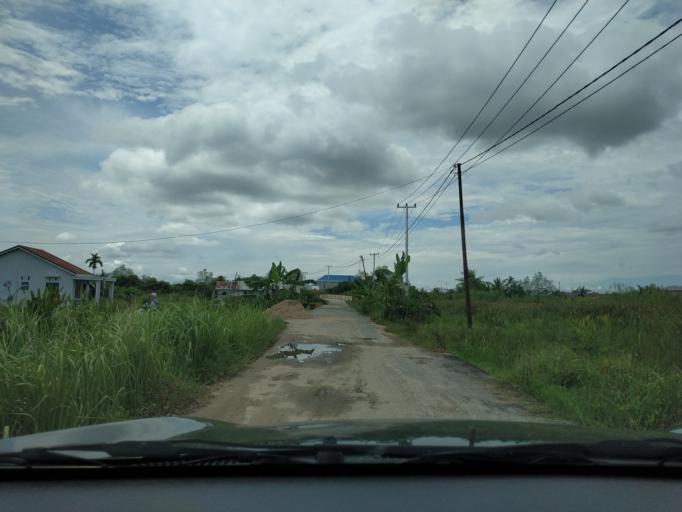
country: ID
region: Riau
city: Tembilahan
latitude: -0.3098
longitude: 103.1796
